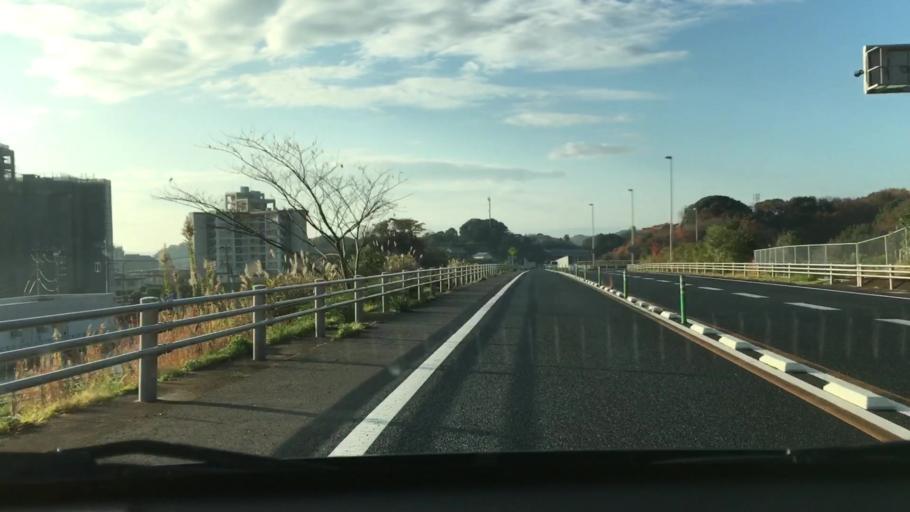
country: JP
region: Nagasaki
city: Sasebo
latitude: 33.0867
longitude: 129.7778
